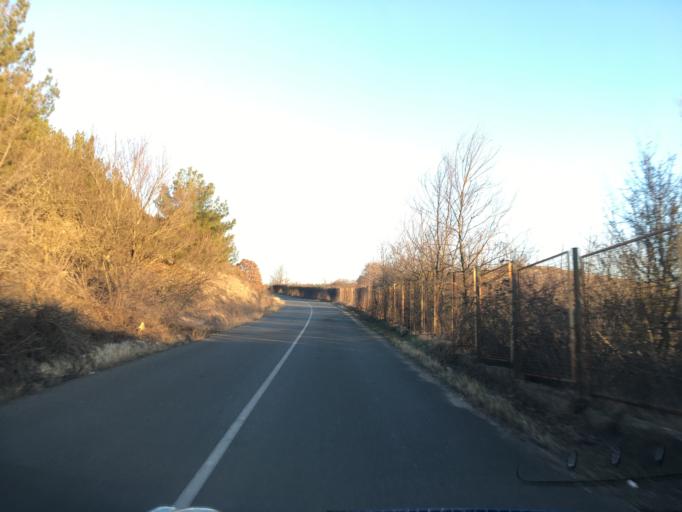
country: GR
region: West Macedonia
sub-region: Nomos Kozanis
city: Koila
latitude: 40.3243
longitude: 21.7938
